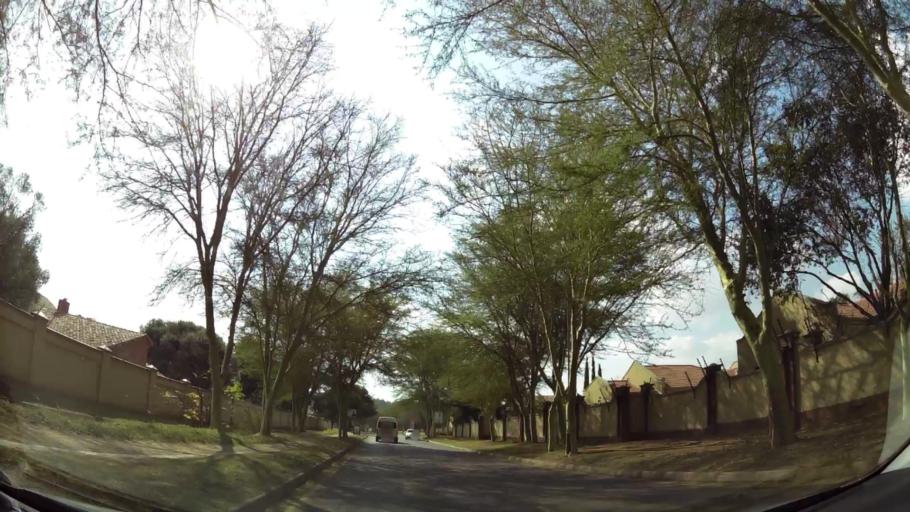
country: ZA
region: Gauteng
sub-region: City of Tshwane Metropolitan Municipality
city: Pretoria
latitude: -25.8026
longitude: 28.3309
